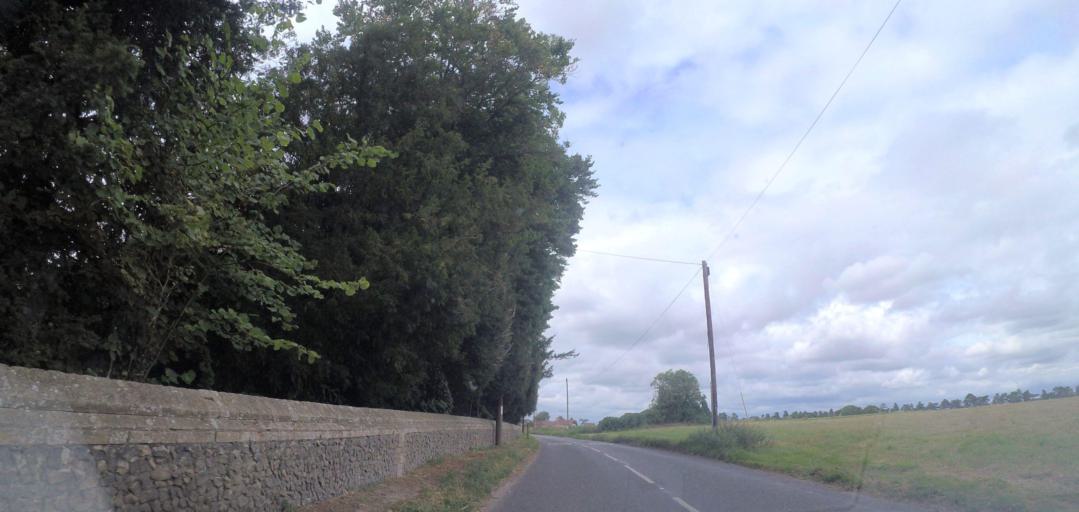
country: GB
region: England
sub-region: Suffolk
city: Lakenheath
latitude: 52.3084
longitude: 0.5513
